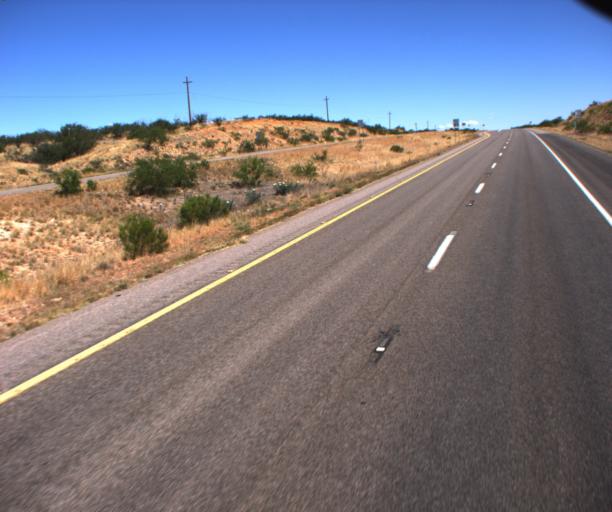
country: US
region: Arizona
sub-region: Cochise County
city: Whetstone
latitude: 31.8416
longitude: -110.3422
